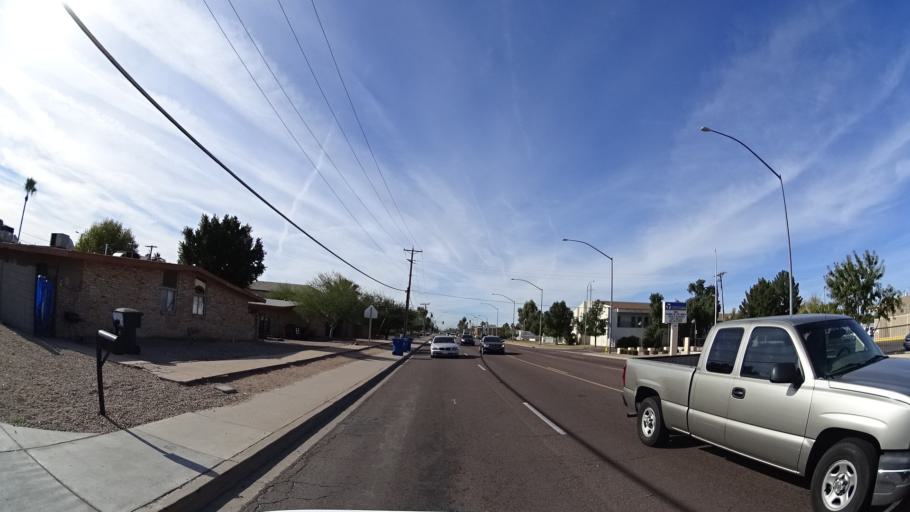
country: US
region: Arizona
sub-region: Maricopa County
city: Mesa
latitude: 33.4081
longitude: -111.7929
